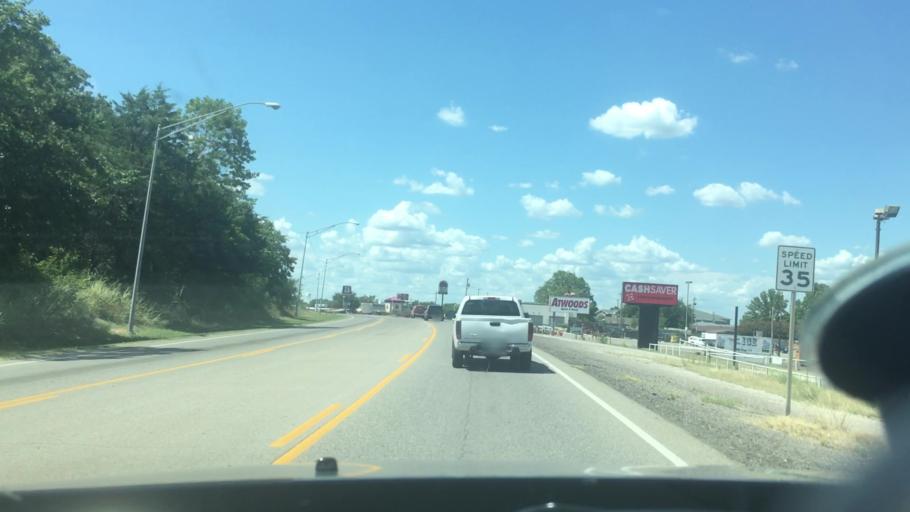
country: US
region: Oklahoma
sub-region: Marshall County
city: Madill
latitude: 34.0775
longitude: -96.7632
